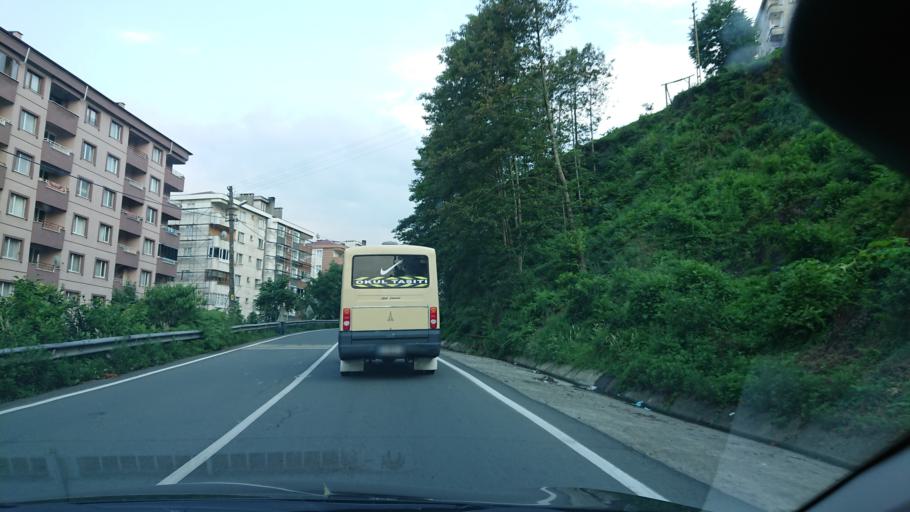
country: TR
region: Rize
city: Cayeli
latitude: 41.0800
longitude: 40.7128
